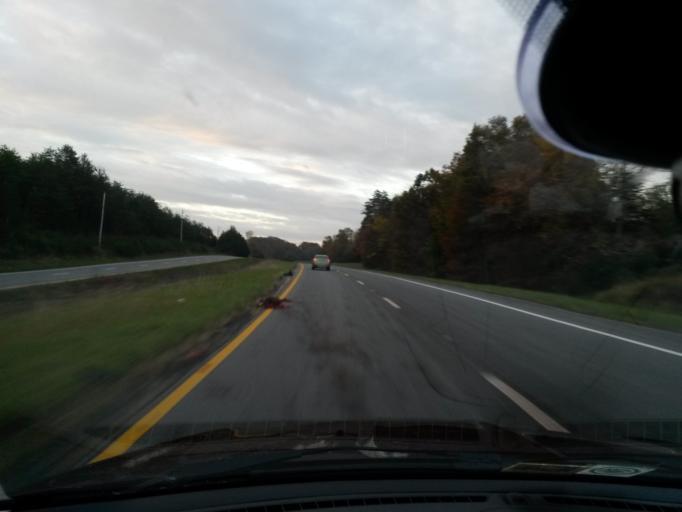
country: US
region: Virginia
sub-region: Botetourt County
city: Fincastle
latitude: 37.5670
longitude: -79.8437
